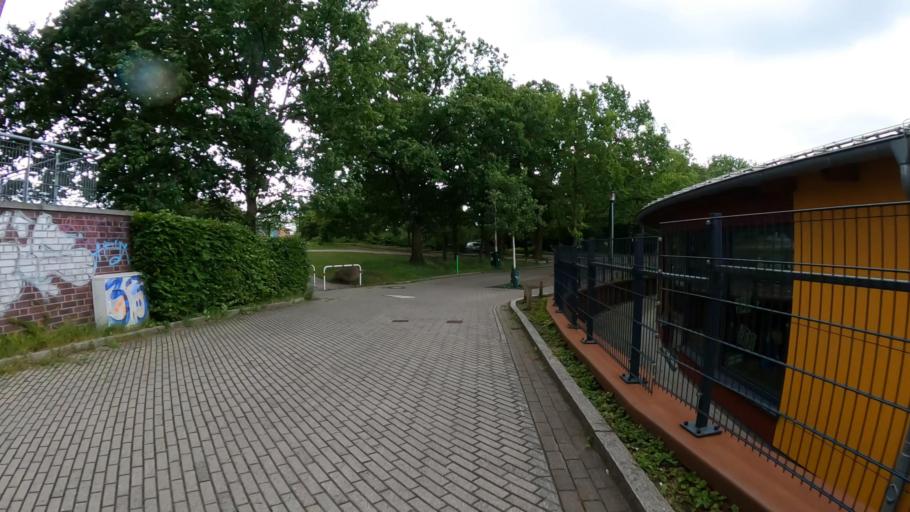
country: DE
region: Schleswig-Holstein
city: Norderstedt
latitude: 53.7063
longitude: 9.9917
